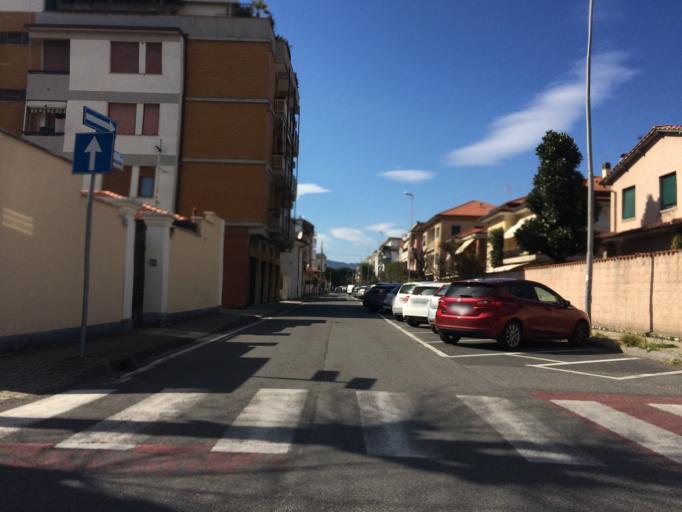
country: IT
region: Tuscany
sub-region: Provincia di Massa-Carrara
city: Marina di Carrara
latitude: 44.0398
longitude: 10.0357
